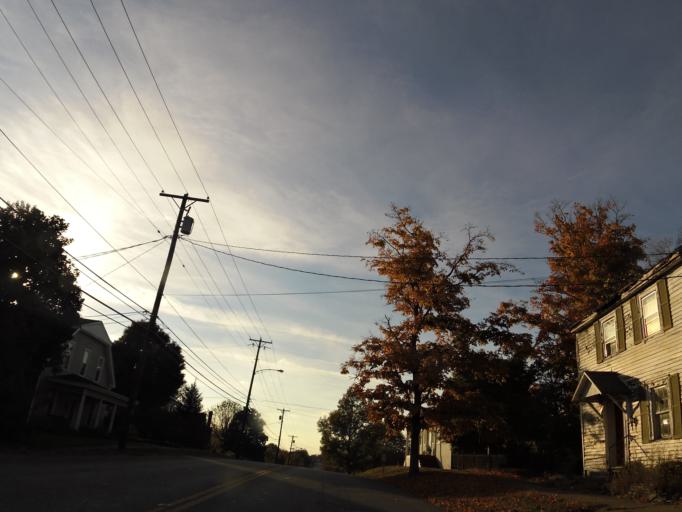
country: US
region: Kentucky
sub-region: Garrard County
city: Lancaster
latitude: 37.6197
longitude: -84.5809
